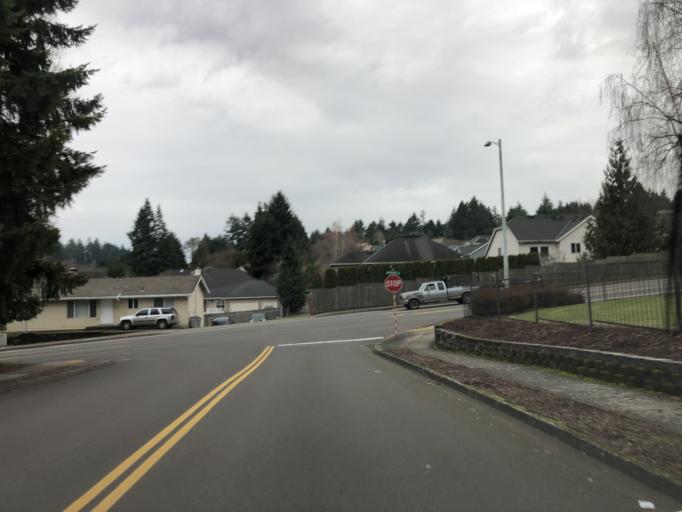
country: US
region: Oregon
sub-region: Washington County
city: King City
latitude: 45.4191
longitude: -122.7954
